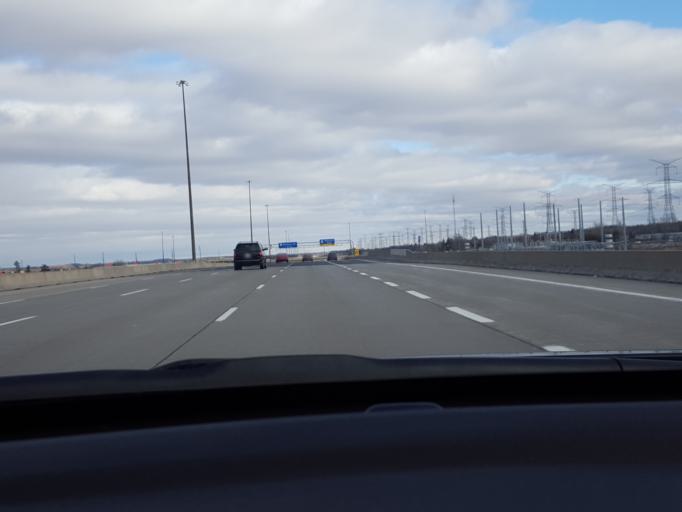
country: CA
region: Ontario
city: Markham
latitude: 43.8479
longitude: -79.3169
